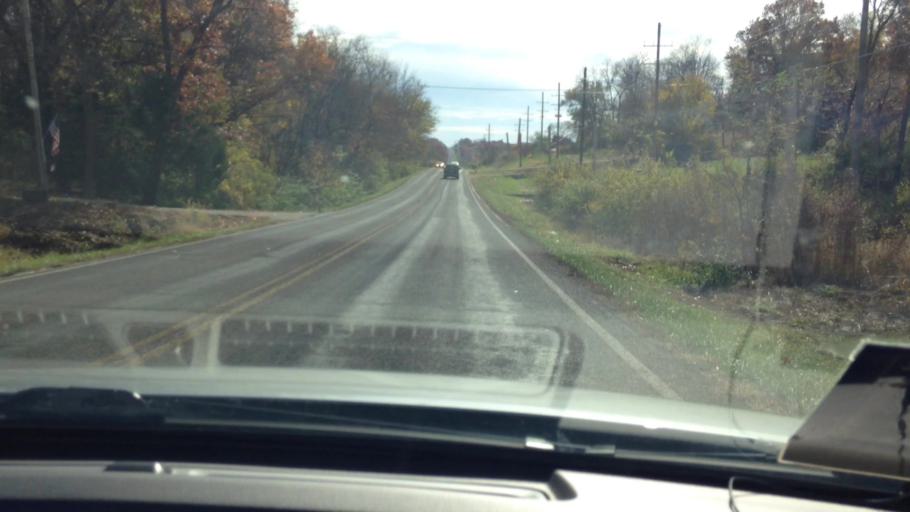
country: US
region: Kansas
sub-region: Leavenworth County
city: Lansing
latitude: 39.2616
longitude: -94.9187
